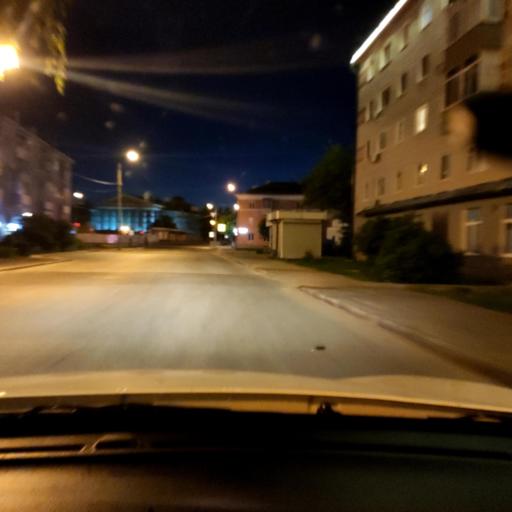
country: RU
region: Tatarstan
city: Osinovo
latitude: 55.8197
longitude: 48.8999
